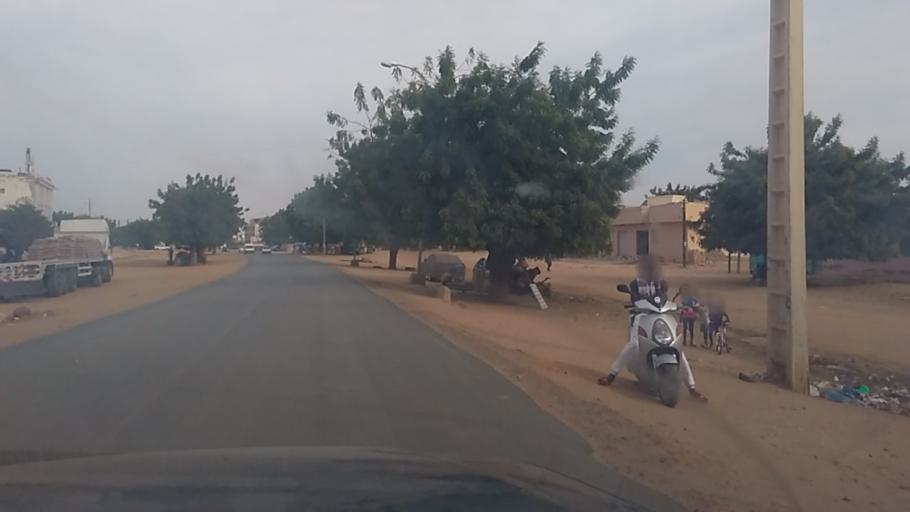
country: SN
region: Diourbel
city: Touba
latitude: 14.8389
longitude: -15.8800
